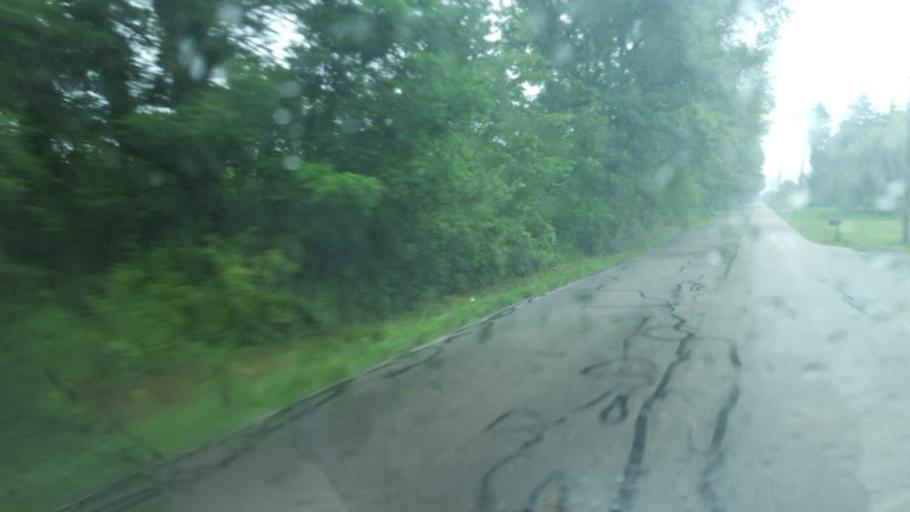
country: US
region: Ohio
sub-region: Delaware County
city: Sunbury
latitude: 40.2412
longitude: -82.9391
